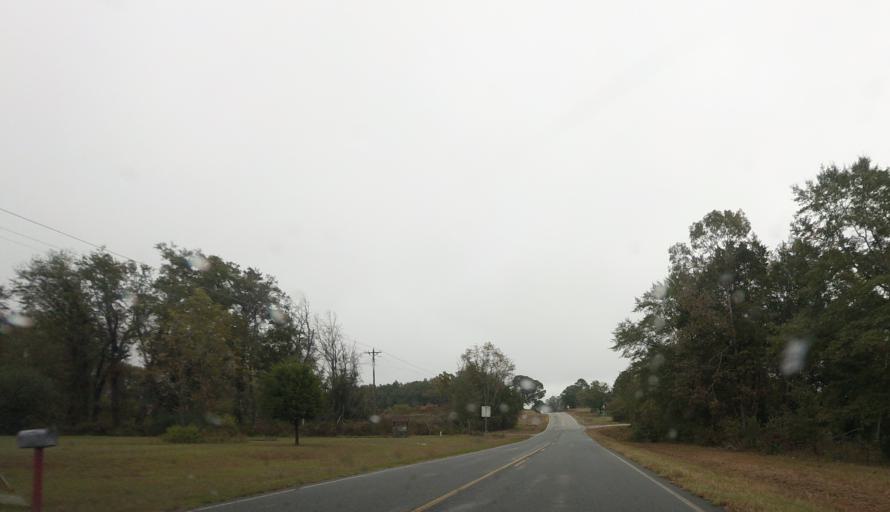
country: US
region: Georgia
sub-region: Marion County
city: Buena Vista
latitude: 32.4201
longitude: -84.3901
